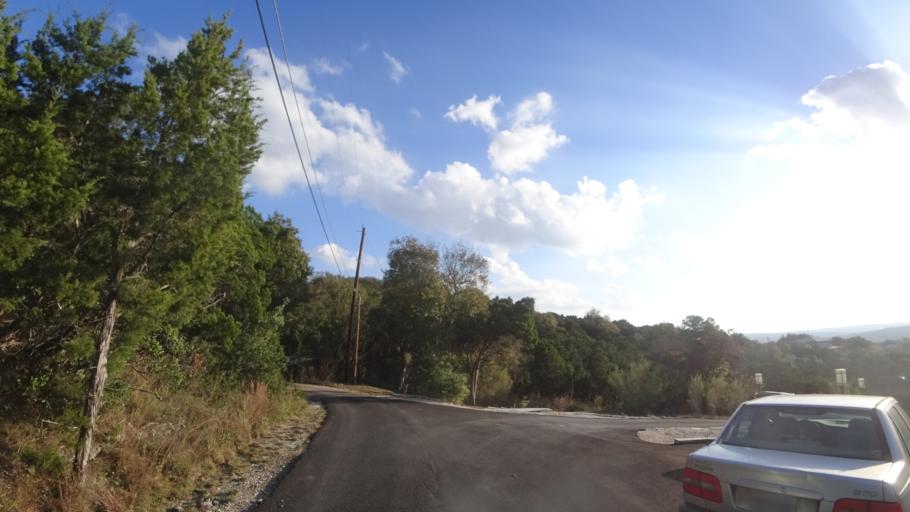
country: US
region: Texas
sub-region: Travis County
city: Lost Creek
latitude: 30.3003
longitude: -97.8411
